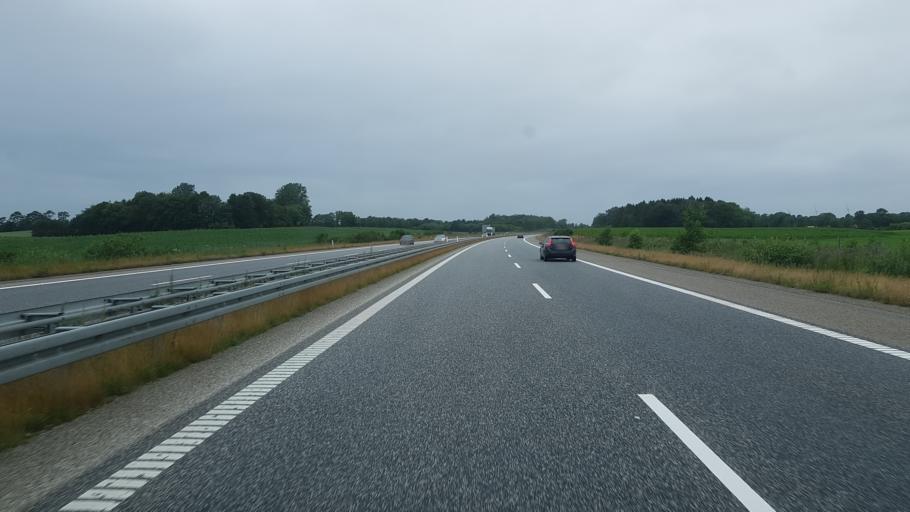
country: DK
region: South Denmark
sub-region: Vejle Kommune
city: Give
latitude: 55.8766
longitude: 9.2359
